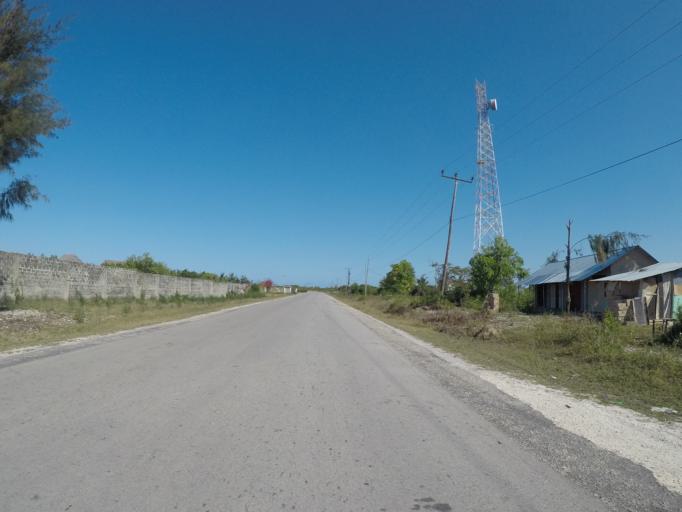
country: TZ
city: Kiwengwa
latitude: -6.1664
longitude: 39.5242
